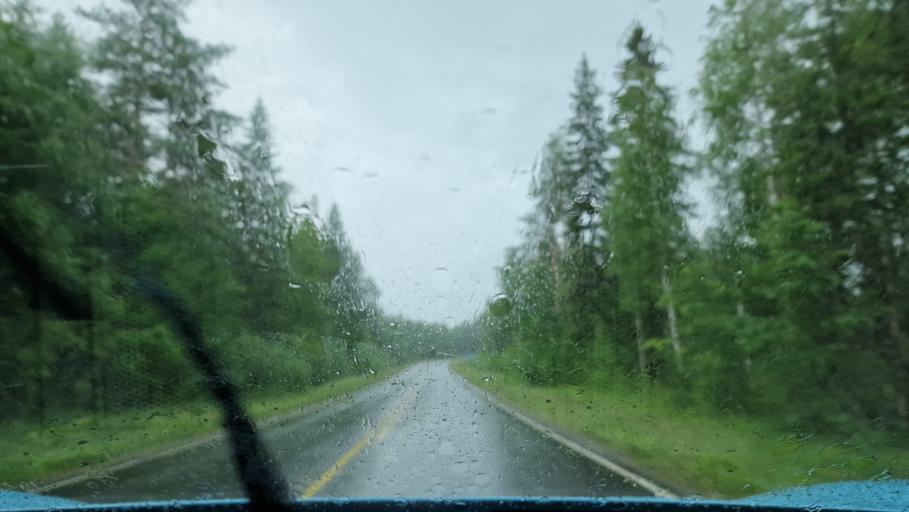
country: FI
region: Southern Ostrobothnia
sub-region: Jaerviseutu
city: Soini
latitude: 62.8251
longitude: 24.3426
